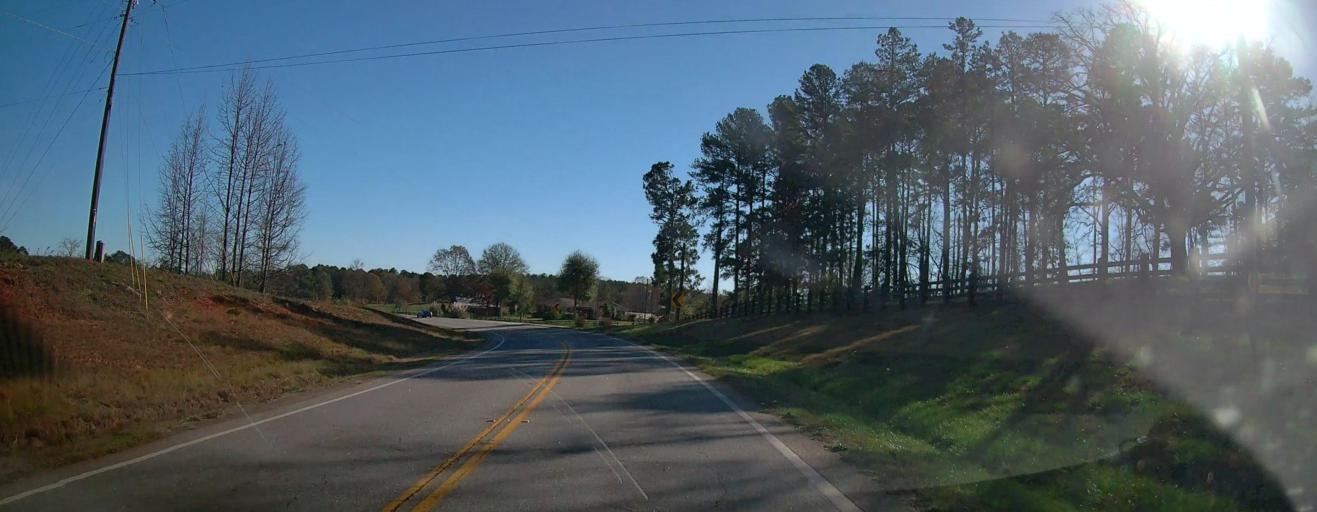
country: US
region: Georgia
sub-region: Hall County
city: Lula
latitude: 34.4456
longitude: -83.7274
